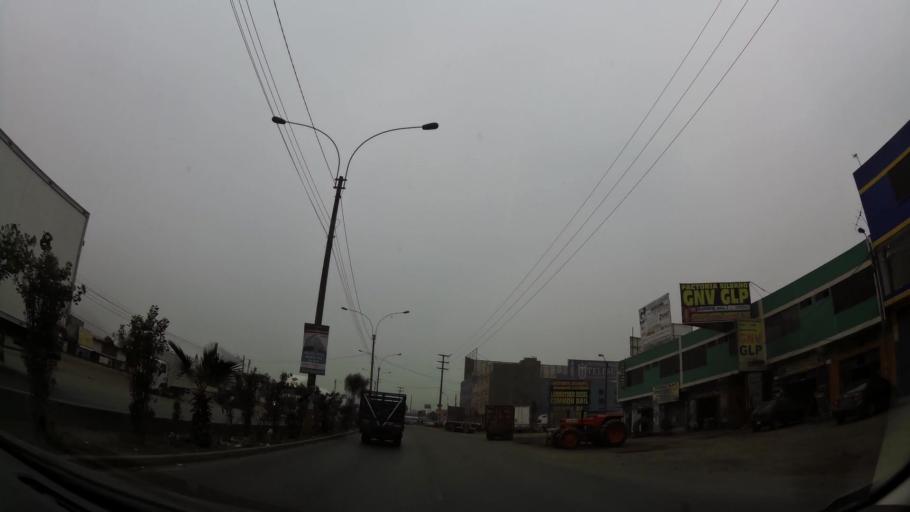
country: PE
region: Lima
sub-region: Lima
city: Santa Maria
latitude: -12.0052
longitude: -76.8454
